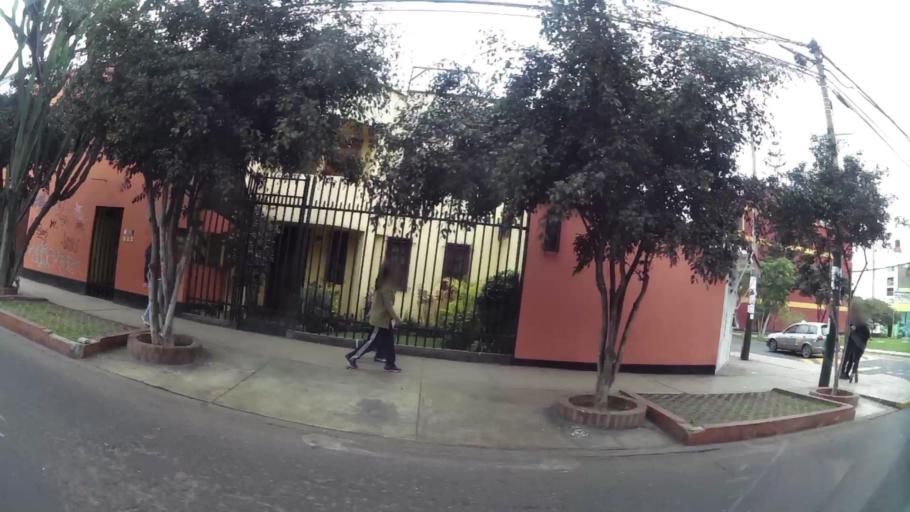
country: PE
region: Lima
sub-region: Lima
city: Surco
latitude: -12.1630
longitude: -76.9960
